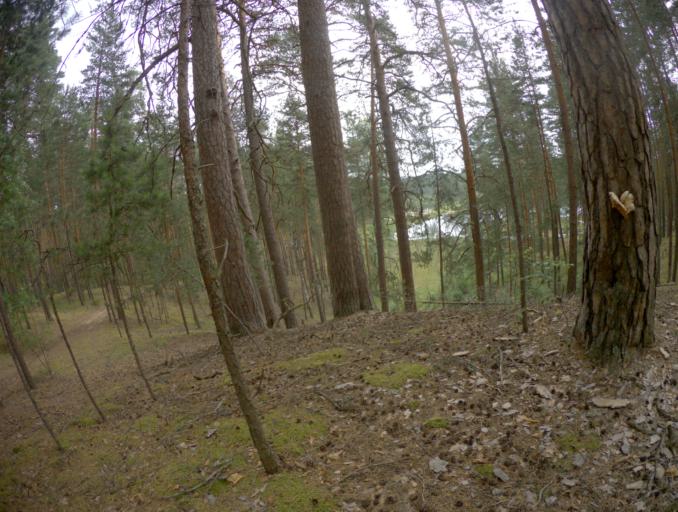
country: RU
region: Nizjnij Novgorod
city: Frolishchi
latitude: 56.3550
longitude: 42.7404
